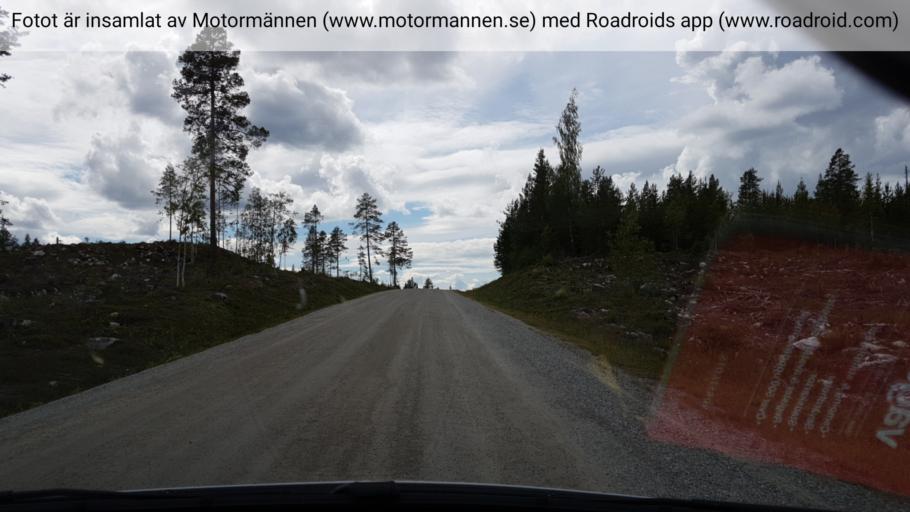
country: SE
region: Vaesternorrland
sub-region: Solleftea Kommun
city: Solleftea
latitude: 63.3423
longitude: 17.4585
